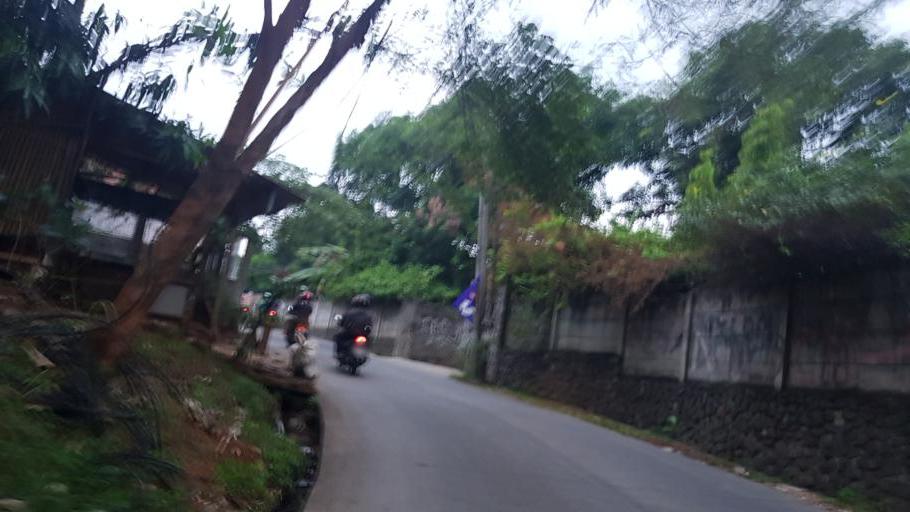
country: ID
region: West Java
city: Depok
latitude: -6.3668
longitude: 106.7948
